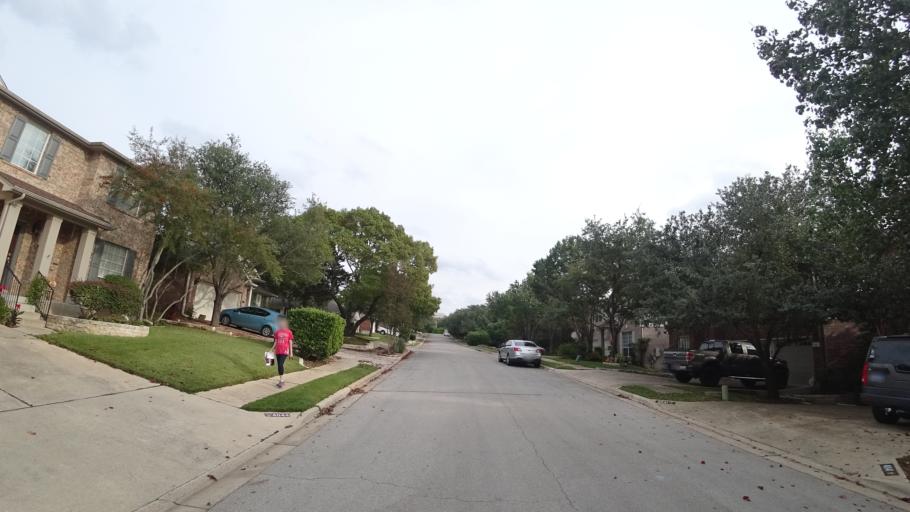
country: US
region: Texas
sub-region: Travis County
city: Hudson Bend
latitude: 30.3809
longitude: -97.8884
